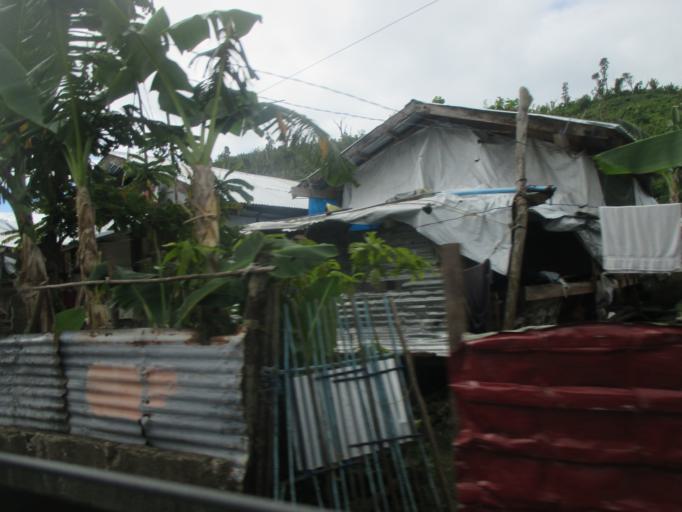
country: PH
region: Eastern Visayas
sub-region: Province of Eastern Samar
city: Lawa-an
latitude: 11.1070
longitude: 125.2109
